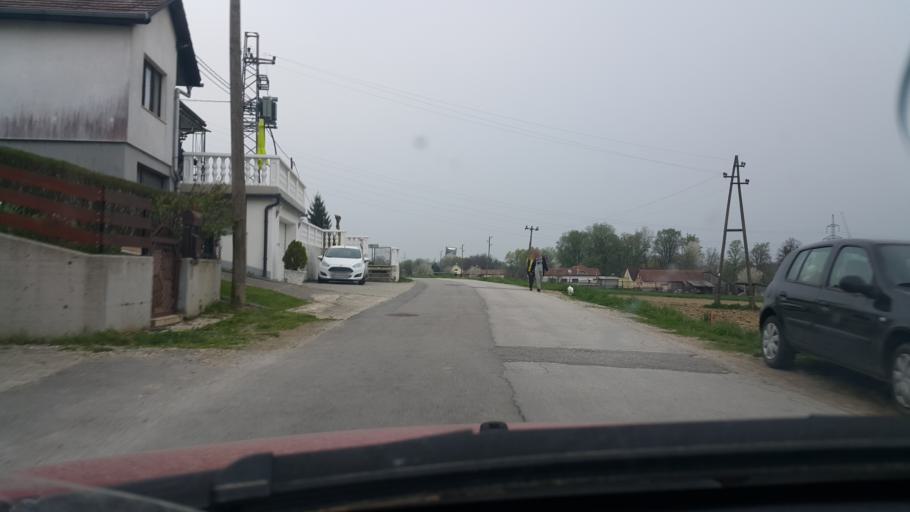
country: SI
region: Duplek
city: Zgornji Duplek
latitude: 46.5222
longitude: 15.7167
